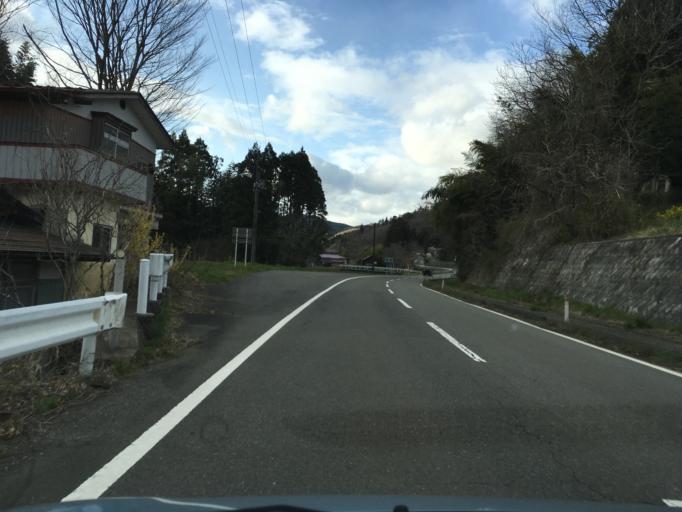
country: JP
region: Iwate
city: Ichinoseki
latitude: 38.7909
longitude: 141.3221
